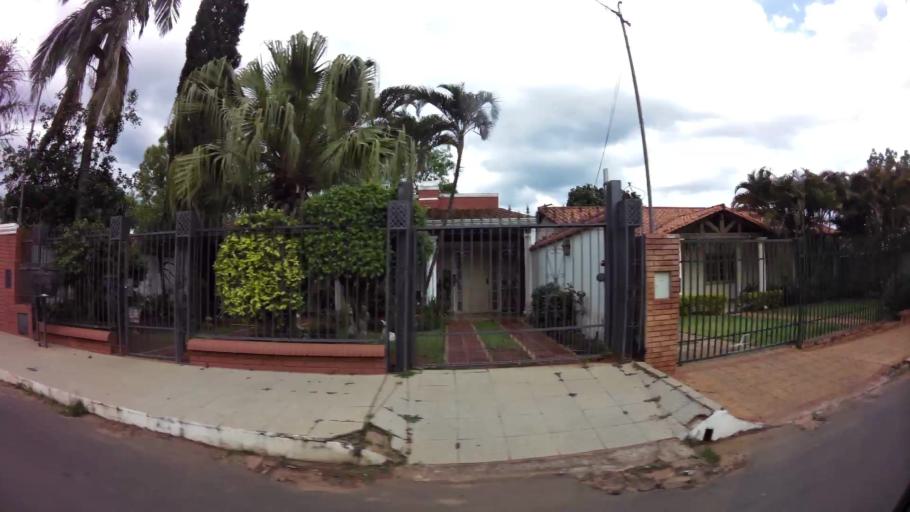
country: PY
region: Central
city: San Lorenzo
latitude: -25.2792
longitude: -57.4913
